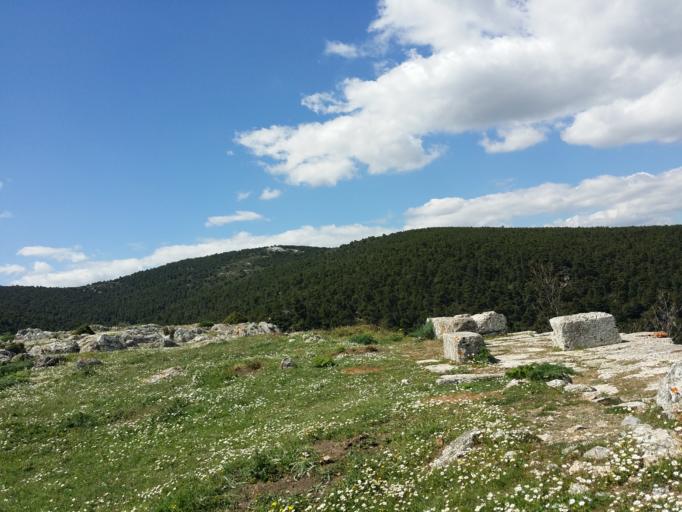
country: GR
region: Attica
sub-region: Nomarchia Dytikis Attikis
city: Fyli
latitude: 38.1400
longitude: 23.6371
